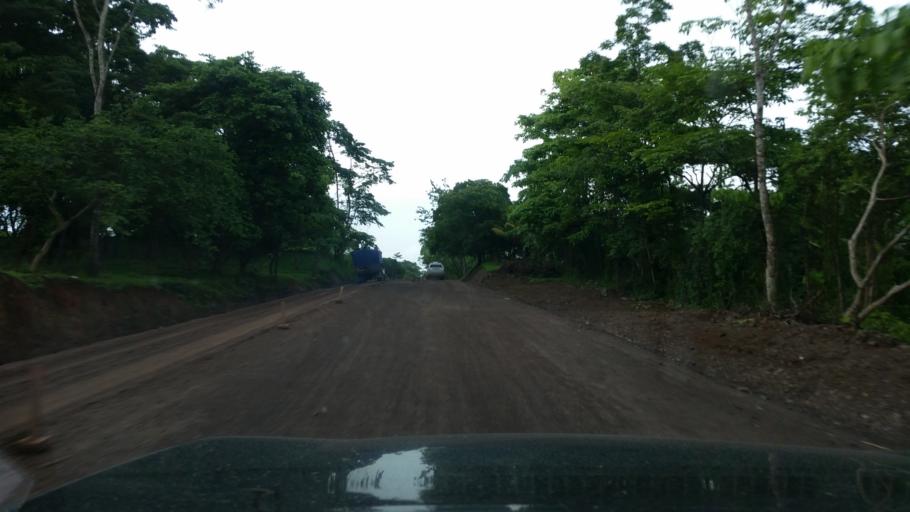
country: NI
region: Matagalpa
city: Rio Blanco
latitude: 13.2594
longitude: -84.9288
